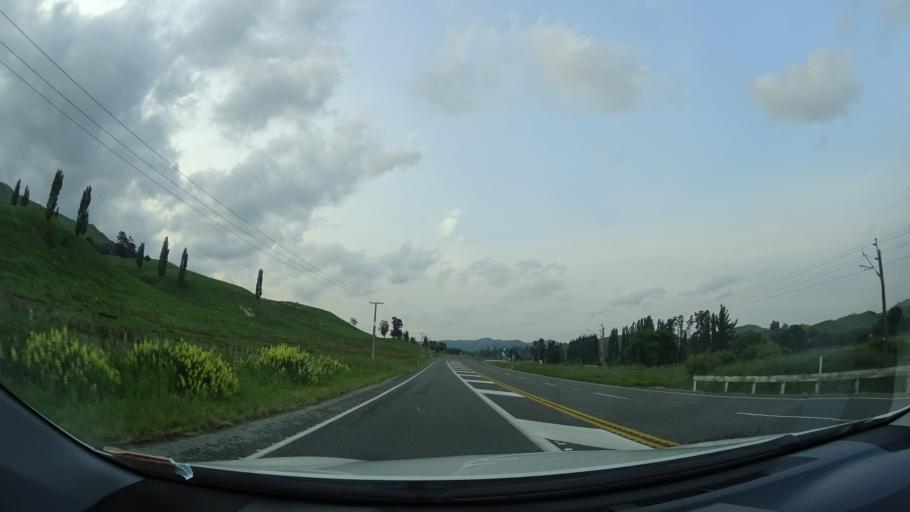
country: NZ
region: Manawatu-Wanganui
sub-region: Ruapehu District
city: Waiouru
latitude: -39.7206
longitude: 175.8407
